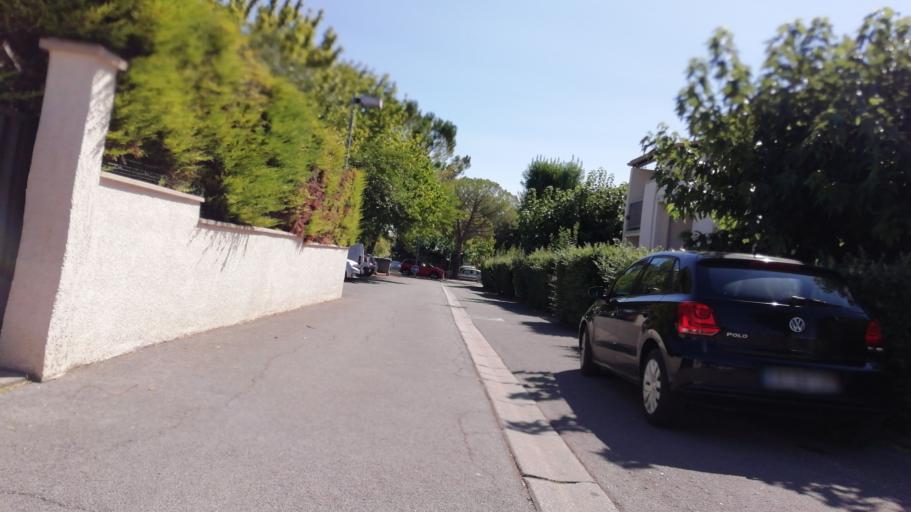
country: FR
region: Languedoc-Roussillon
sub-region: Departement de l'Herault
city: Saint-Martin-de-Londres
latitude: 43.7885
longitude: 3.7297
